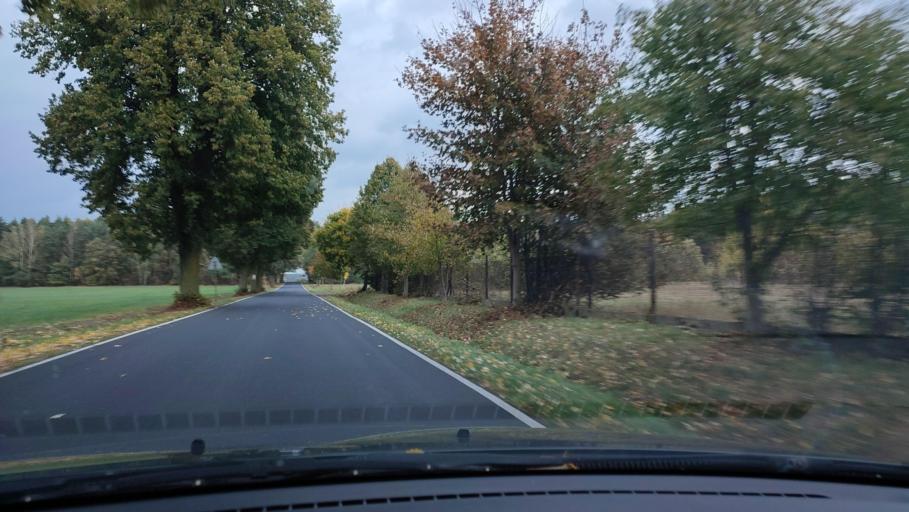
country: PL
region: Masovian Voivodeship
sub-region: Powiat mlawski
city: Wieczfnia Koscielna
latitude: 53.2162
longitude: 20.4053
